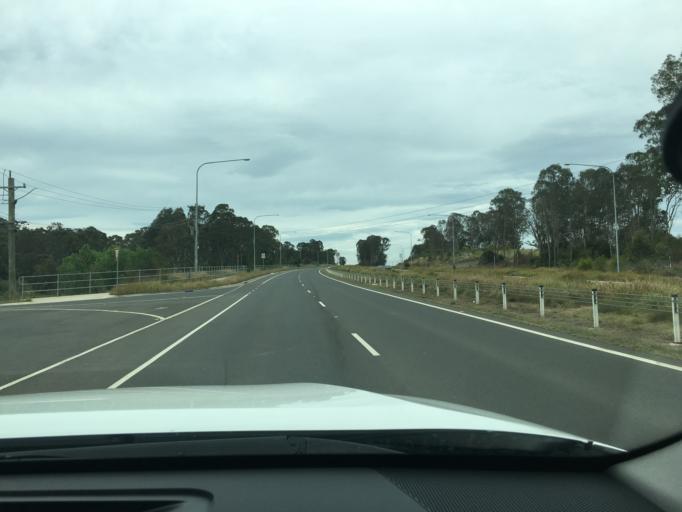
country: AU
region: New South Wales
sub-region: Campbelltown Municipality
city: Denham Court
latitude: -33.9898
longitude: 150.7907
